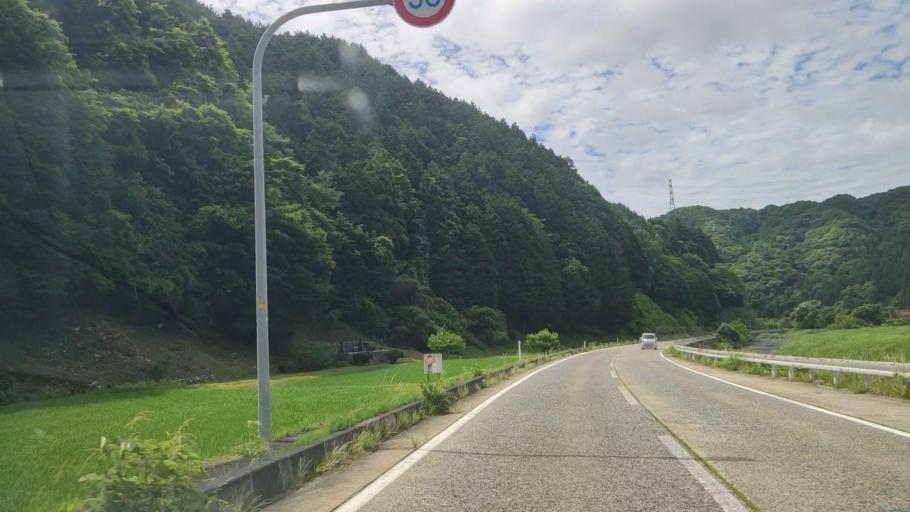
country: JP
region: Okayama
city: Niimi
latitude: 35.1680
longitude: 133.5799
